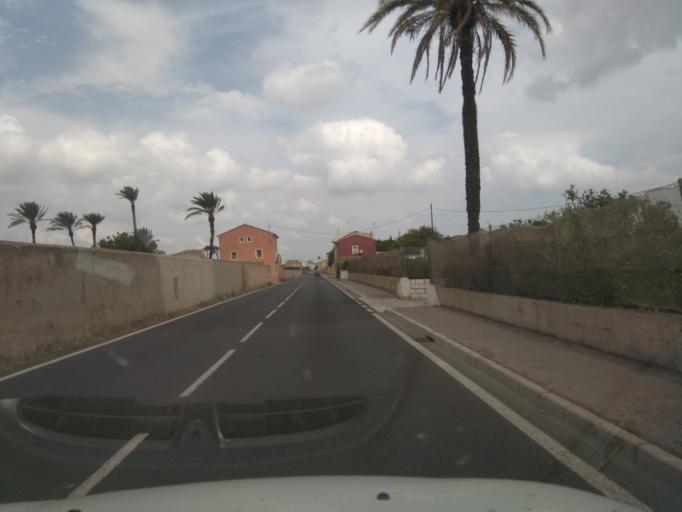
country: ES
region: Valencia
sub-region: Provincia de Valencia
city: Carcaixent
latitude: 39.1370
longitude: -0.4424
